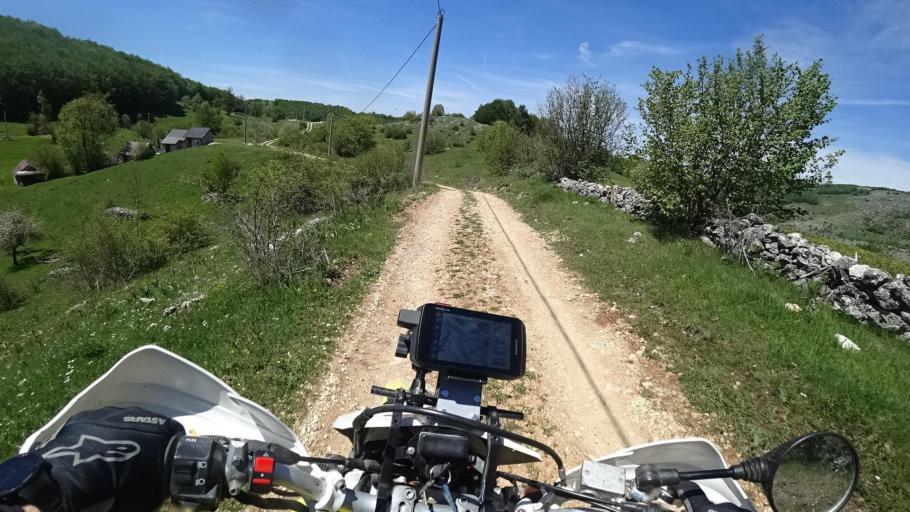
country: BA
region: Federation of Bosnia and Herzegovina
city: Polje-Bijela
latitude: 43.6463
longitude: 18.0594
